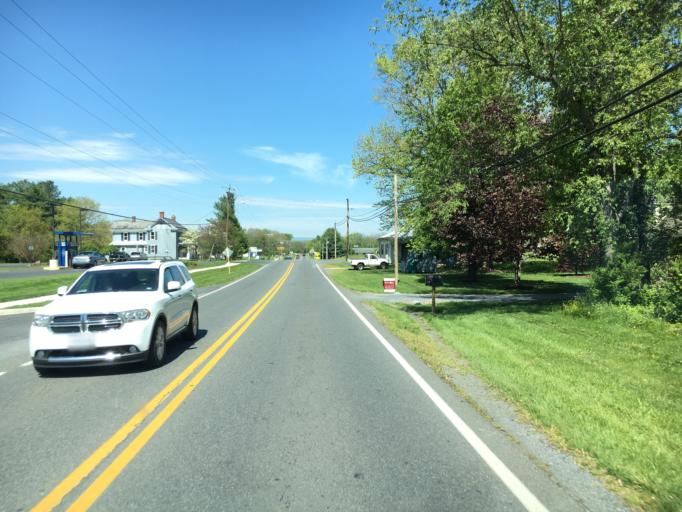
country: US
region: Virginia
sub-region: Rockingham County
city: Grottoes
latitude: 38.2624
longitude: -78.8257
